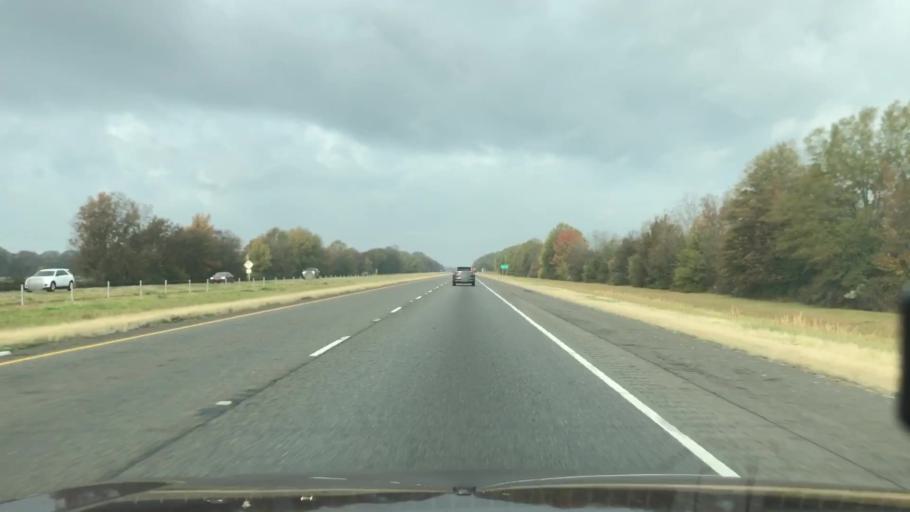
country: US
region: Louisiana
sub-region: Richland Parish
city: Delhi
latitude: 32.4335
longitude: -91.4320
